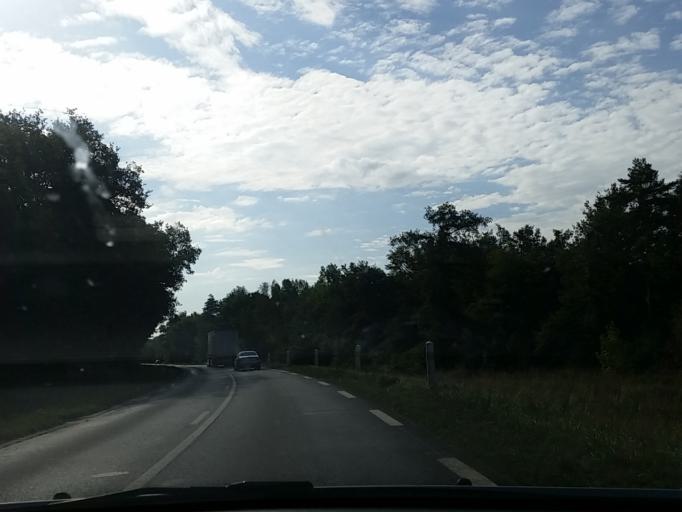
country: FR
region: Centre
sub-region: Departement du Loir-et-Cher
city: Romorantin-Lanthenay
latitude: 47.3751
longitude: 1.6906
